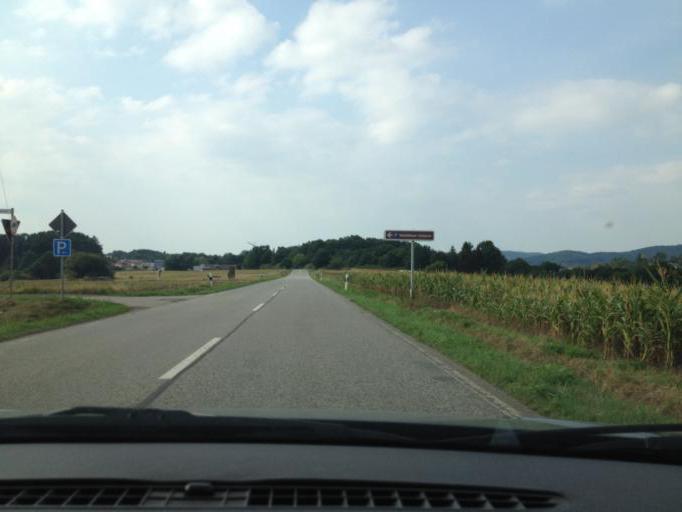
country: DE
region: Saarland
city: Sankt Wendel
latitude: 49.4852
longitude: 7.1645
